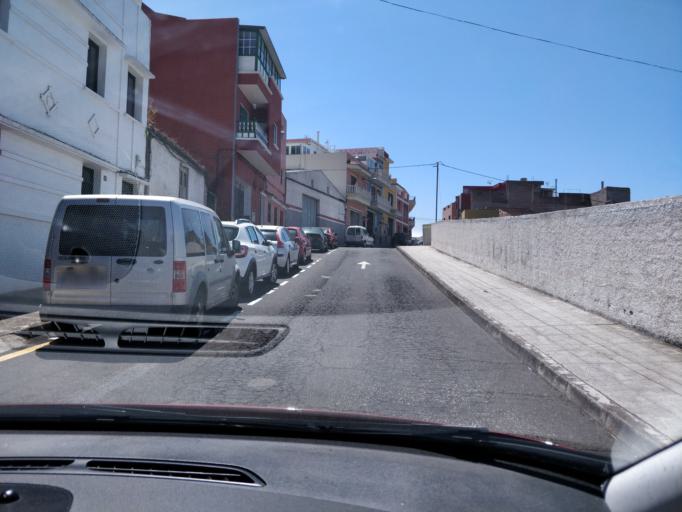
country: ES
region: Canary Islands
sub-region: Provincia de Santa Cruz de Tenerife
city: La Orotava
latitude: 28.3846
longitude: -16.5198
